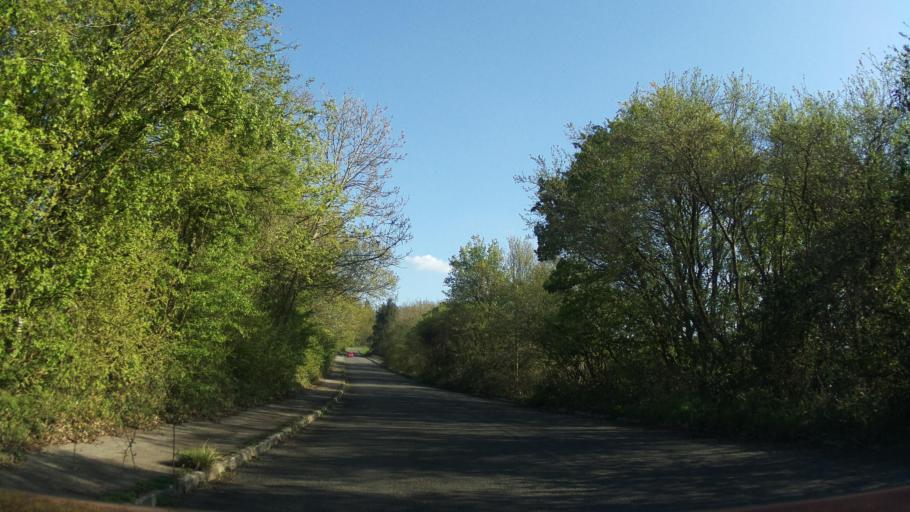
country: GB
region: England
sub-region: South Gloucestershire
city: Falfield
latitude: 51.6543
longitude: -2.4382
